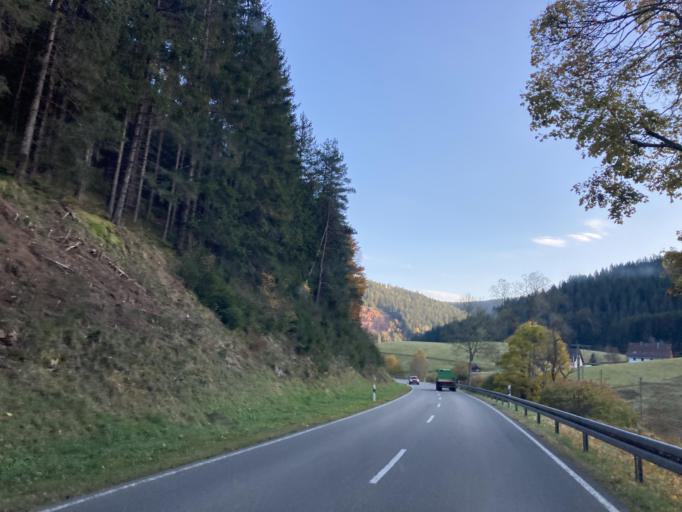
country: DE
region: Baden-Wuerttemberg
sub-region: Freiburg Region
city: Vohrenbach
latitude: 47.9985
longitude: 8.3046
